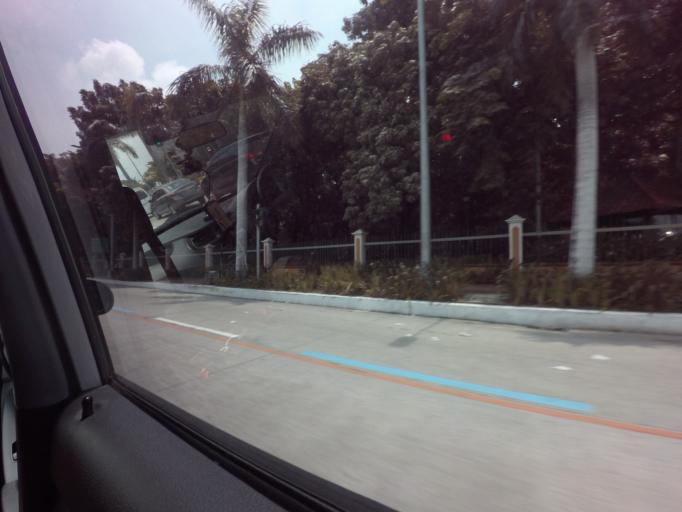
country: PH
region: Metro Manila
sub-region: City of Manila
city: Port Area
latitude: 14.5819
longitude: 120.9762
